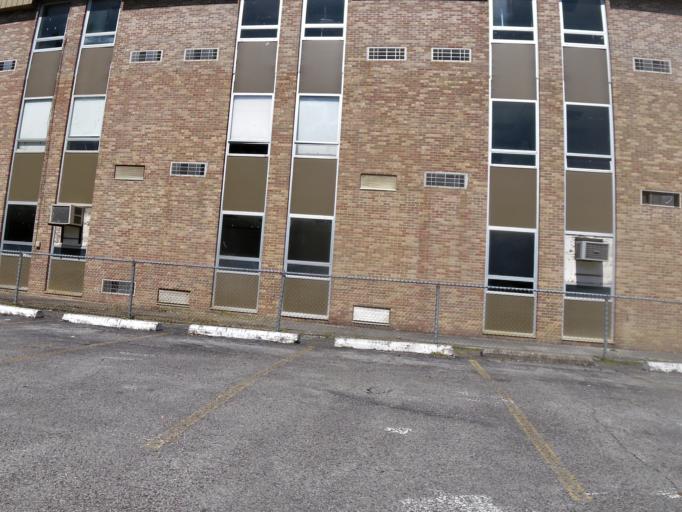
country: US
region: Kentucky
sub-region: Leslie County
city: Hyden
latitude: 37.1635
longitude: -83.3770
